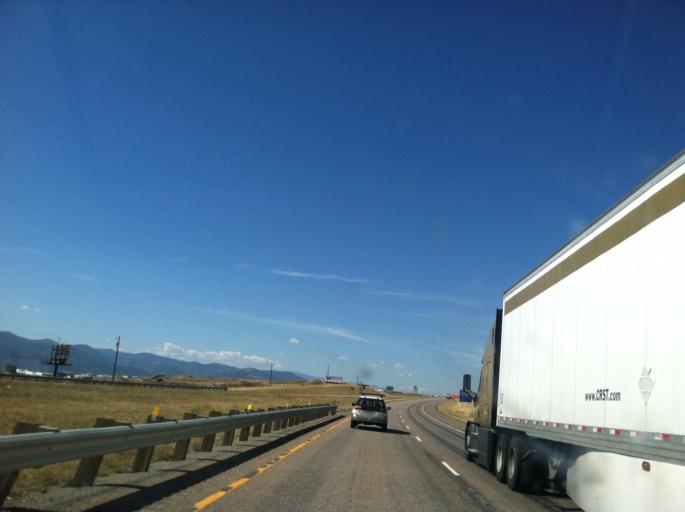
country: US
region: Montana
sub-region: Missoula County
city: Orchard Homes
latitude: 46.9407
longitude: -114.1120
